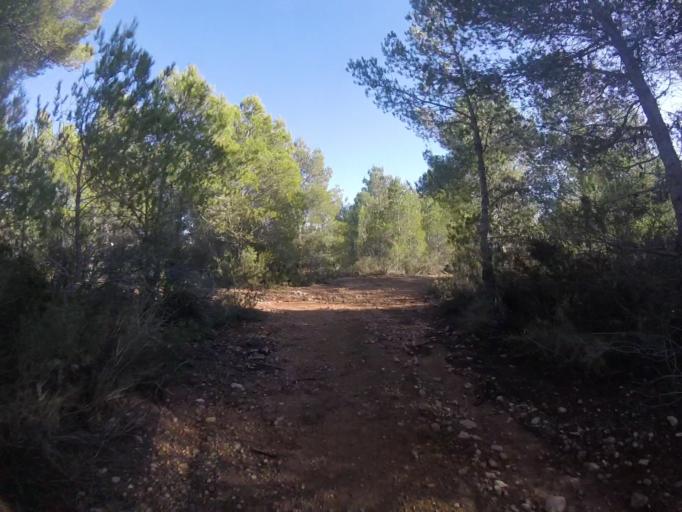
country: ES
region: Valencia
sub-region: Provincia de Castello
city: Sarratella
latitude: 40.2861
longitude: 0.0637
